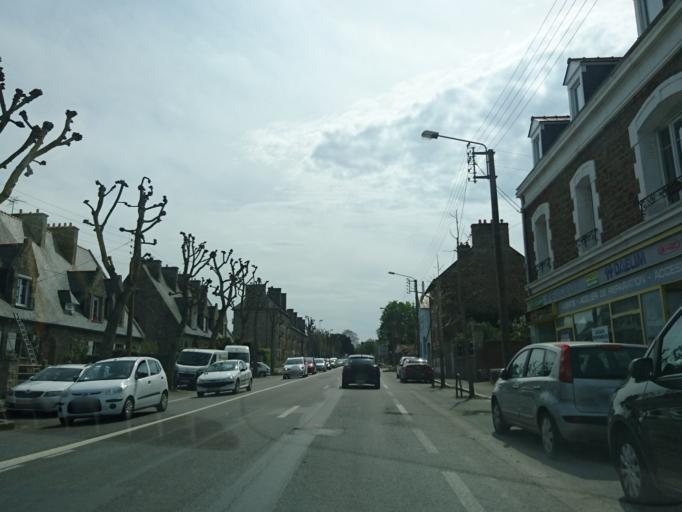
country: FR
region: Brittany
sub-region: Departement d'Ille-et-Vilaine
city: Saint-Malo
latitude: 48.6324
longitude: -2.0071
